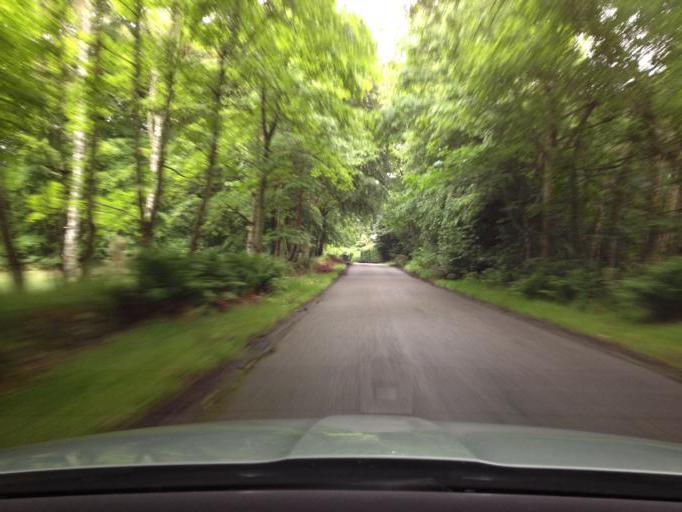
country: GB
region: Scotland
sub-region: Angus
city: Brechin
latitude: 56.8338
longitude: -2.6544
